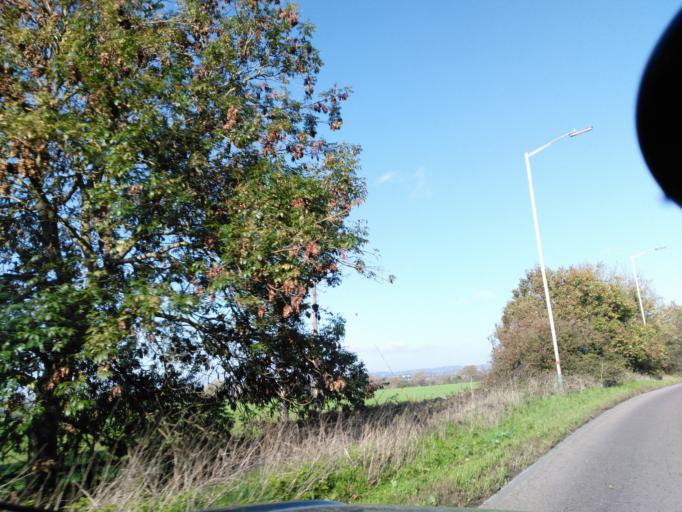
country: GB
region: England
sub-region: Wiltshire
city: Melksham
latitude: 51.3669
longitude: -2.1458
